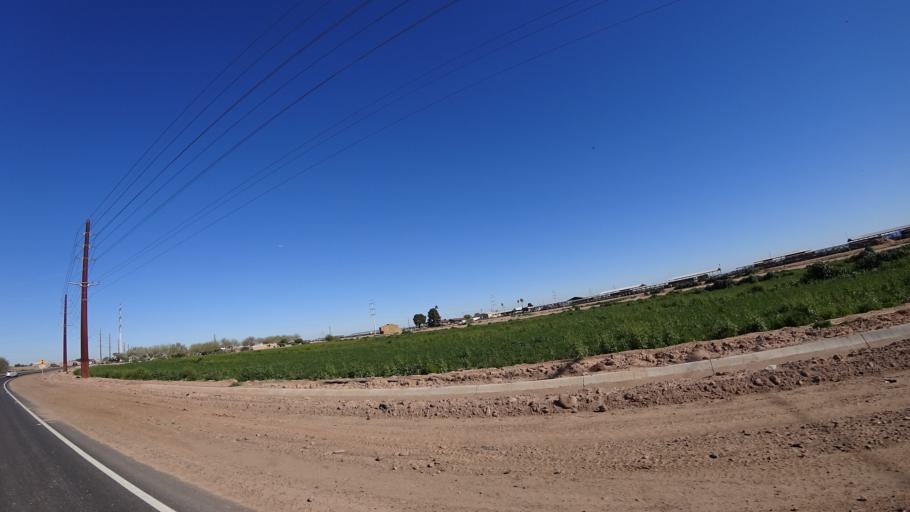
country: US
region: Arizona
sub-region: Maricopa County
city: Tolleson
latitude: 33.4041
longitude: -112.2545
